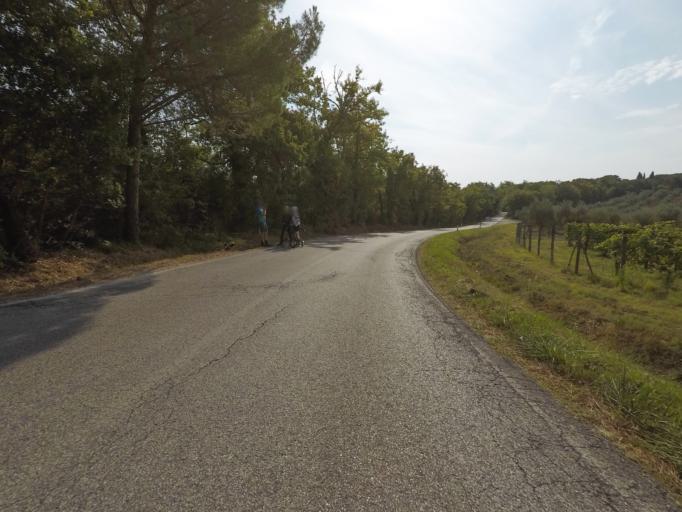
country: IT
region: Tuscany
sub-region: Provincia di Siena
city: Radda in Chianti
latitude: 43.4129
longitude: 11.3516
